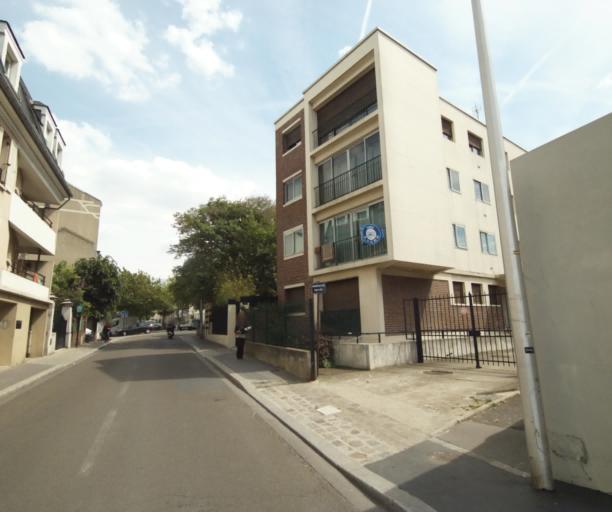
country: FR
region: Ile-de-France
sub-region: Departement des Hauts-de-Seine
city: Colombes
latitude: 48.9231
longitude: 2.2585
